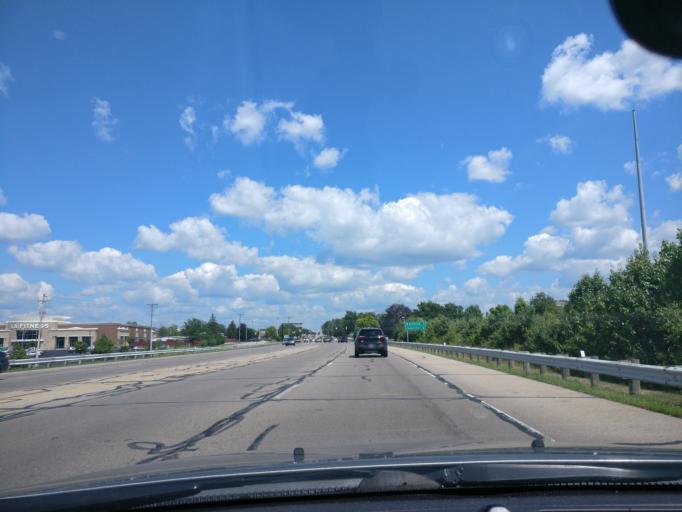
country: US
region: Ohio
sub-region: Montgomery County
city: Centerville
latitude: 39.6438
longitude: -84.1614
